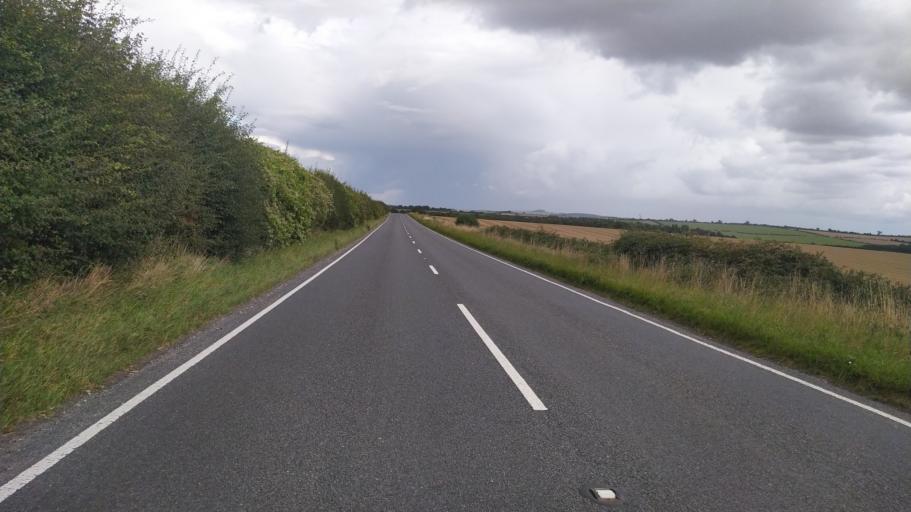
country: GB
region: England
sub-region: Dorset
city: Blandford Forum
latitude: 50.9036
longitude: -2.0750
